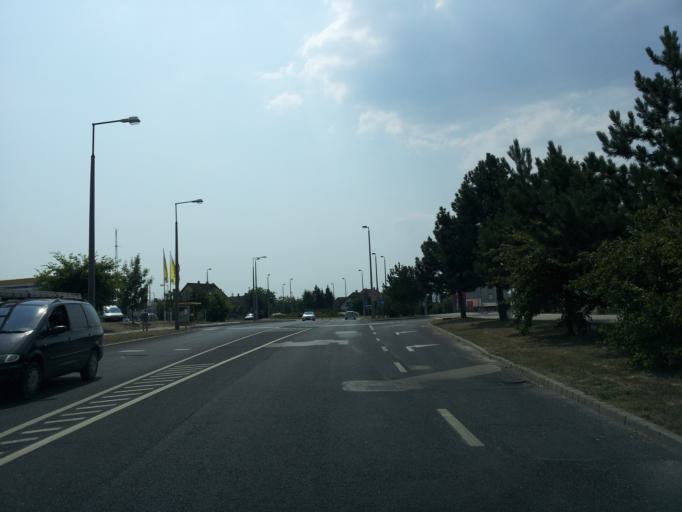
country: HU
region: Veszprem
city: Veszprem
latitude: 47.0863
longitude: 17.9211
